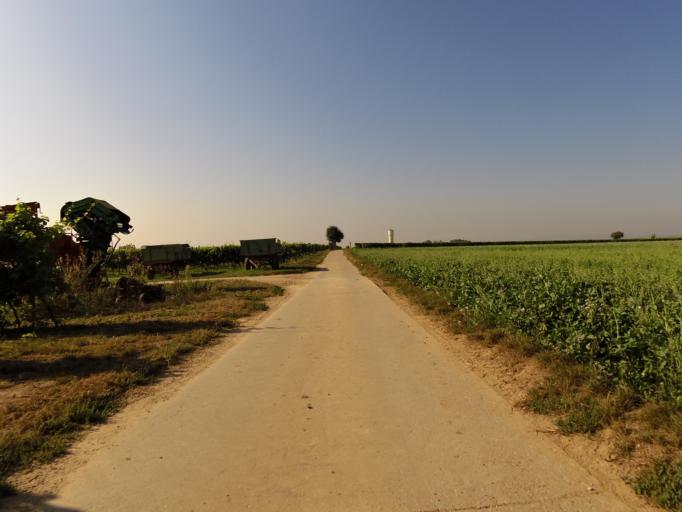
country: DE
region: Rheinland-Pfalz
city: Kleinniedesheim
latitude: 49.5859
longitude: 8.3183
